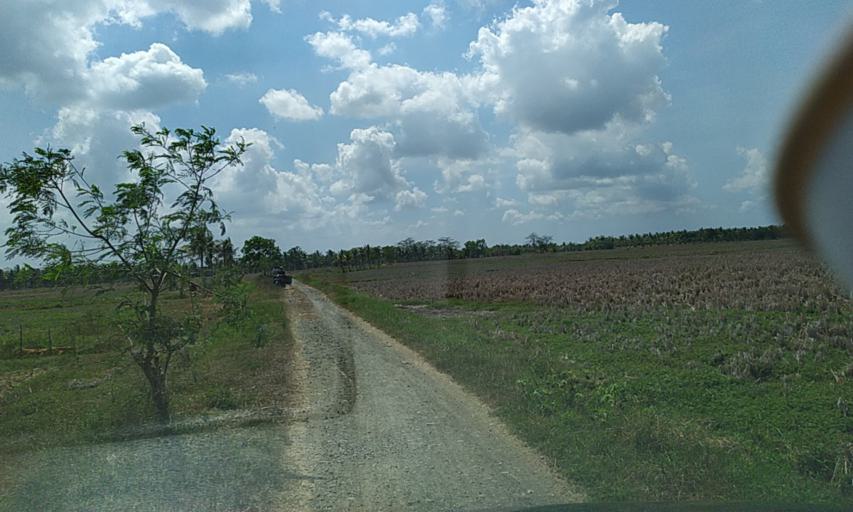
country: ID
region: Central Java
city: Cimrutu
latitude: -7.6249
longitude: 108.8165
